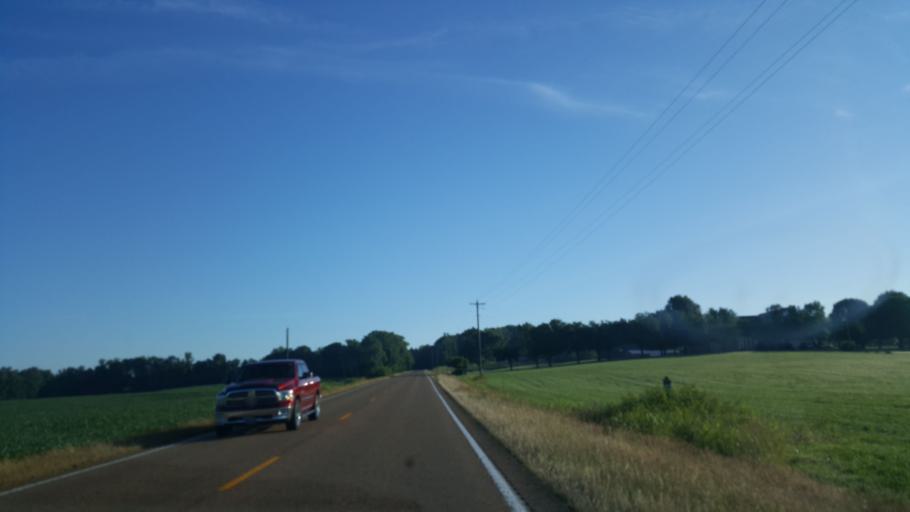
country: US
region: Tennessee
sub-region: McNairy County
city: Adamsville
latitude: 35.4411
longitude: -88.3718
